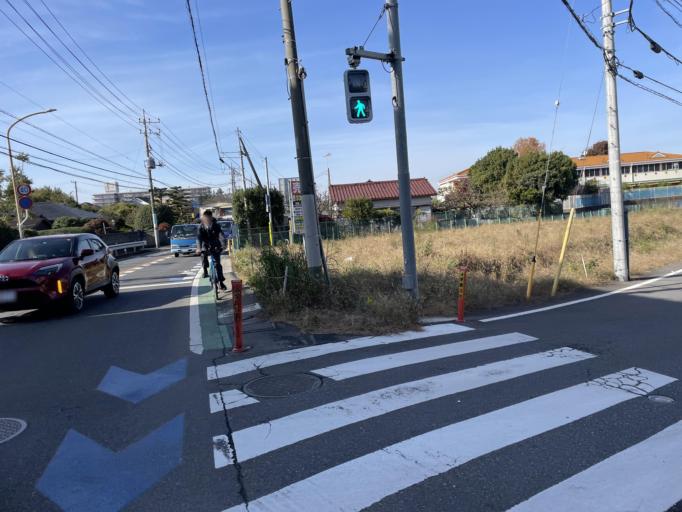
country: JP
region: Chiba
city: Kashiwa
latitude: 35.7778
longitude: 139.9882
